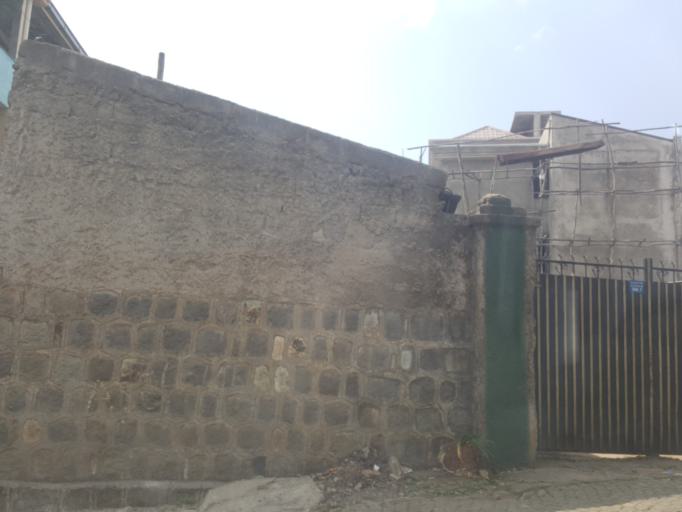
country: ET
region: Adis Abeba
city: Addis Ababa
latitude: 9.0597
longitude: 38.7200
